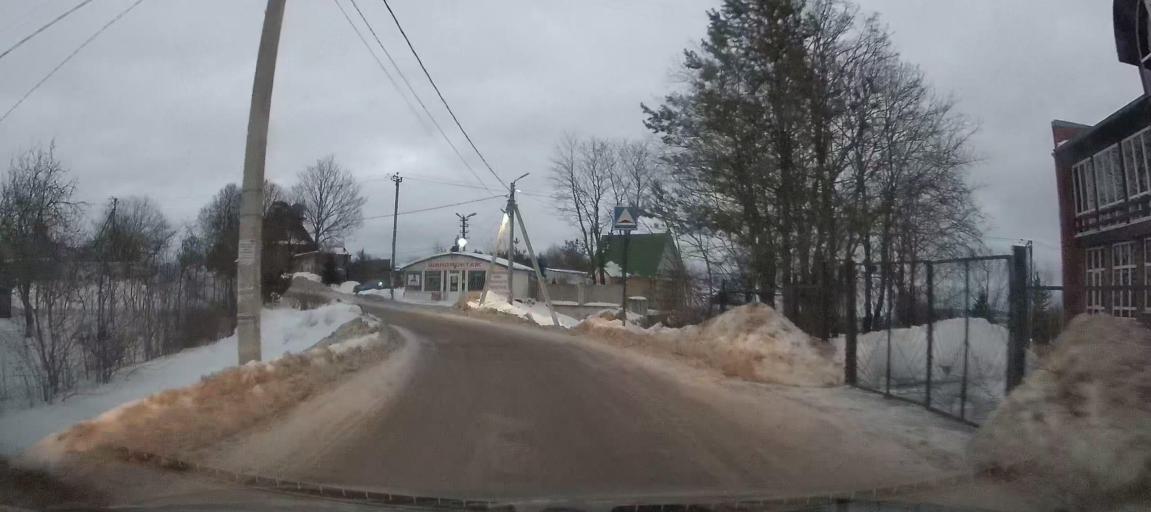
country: RU
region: Leningrad
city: Taytsy
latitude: 59.6972
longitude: 30.1397
